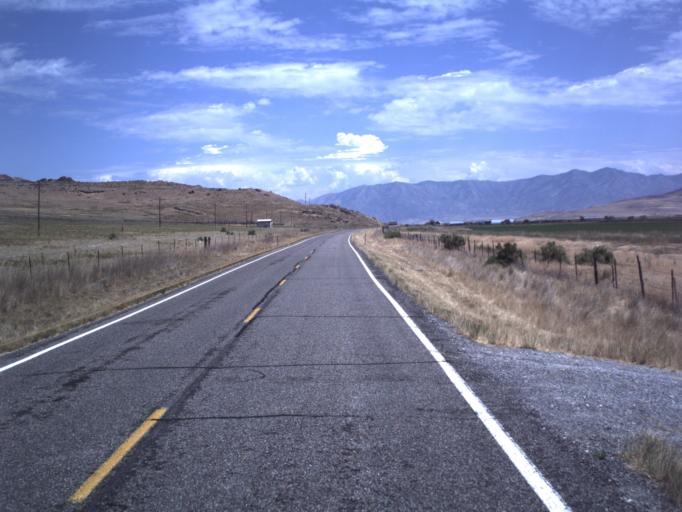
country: US
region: Utah
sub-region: Box Elder County
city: Tremonton
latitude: 41.6204
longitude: -112.3592
